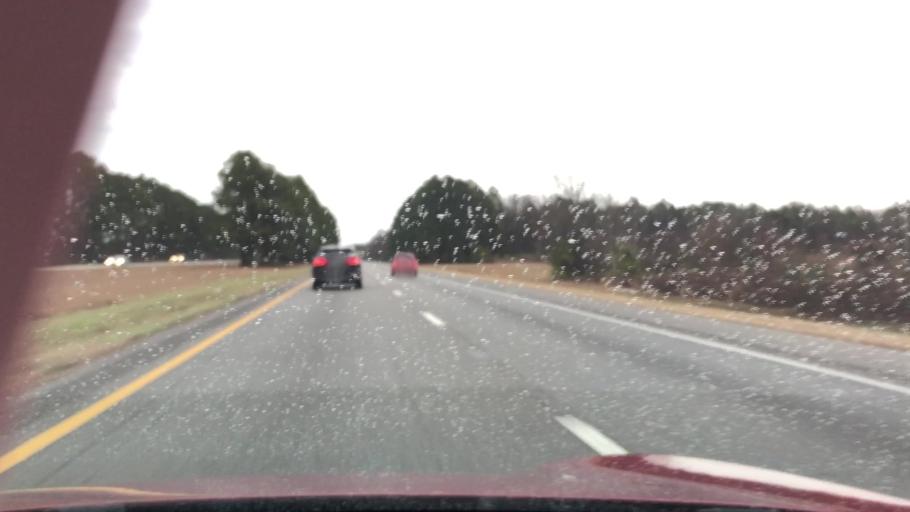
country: US
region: South Carolina
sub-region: Dillon County
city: Latta
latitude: 34.3749
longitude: -79.4847
